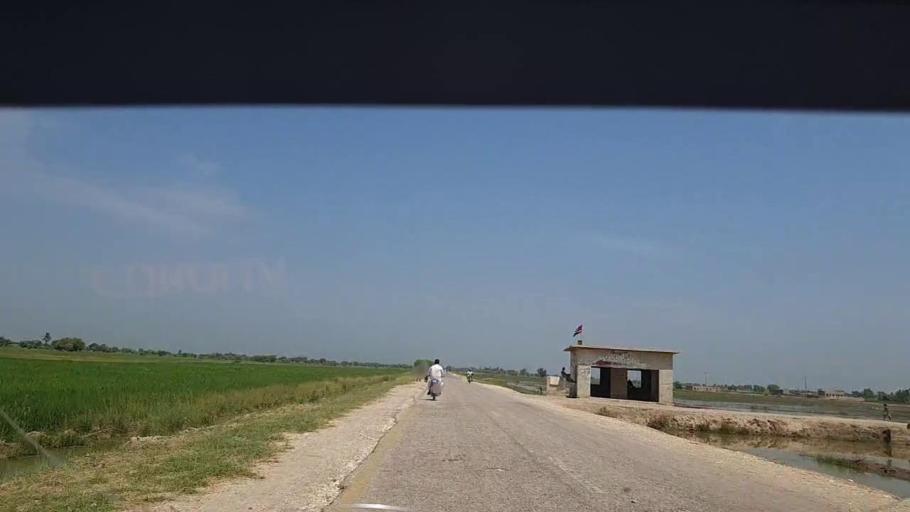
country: PK
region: Sindh
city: Rustam jo Goth
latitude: 28.0971
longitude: 68.8015
